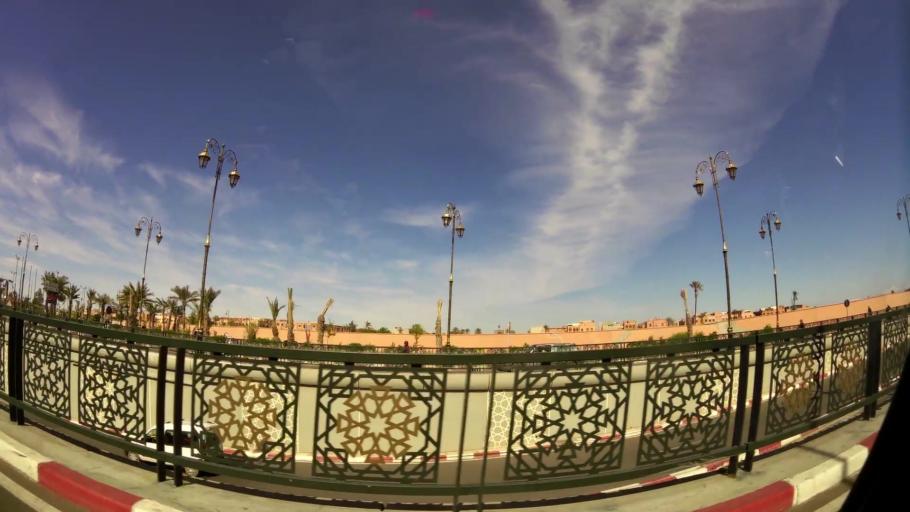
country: MA
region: Marrakech-Tensift-Al Haouz
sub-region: Marrakech
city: Marrakesh
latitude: 31.6439
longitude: -7.9871
